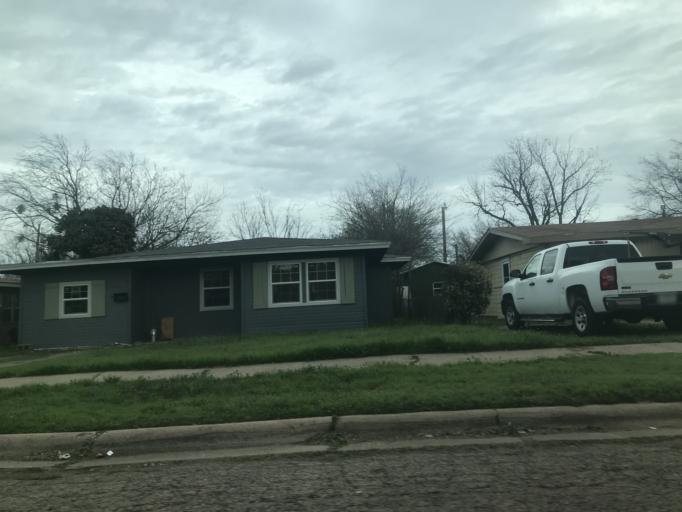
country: US
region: Texas
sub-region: Taylor County
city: Abilene
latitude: 32.4642
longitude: -99.7480
